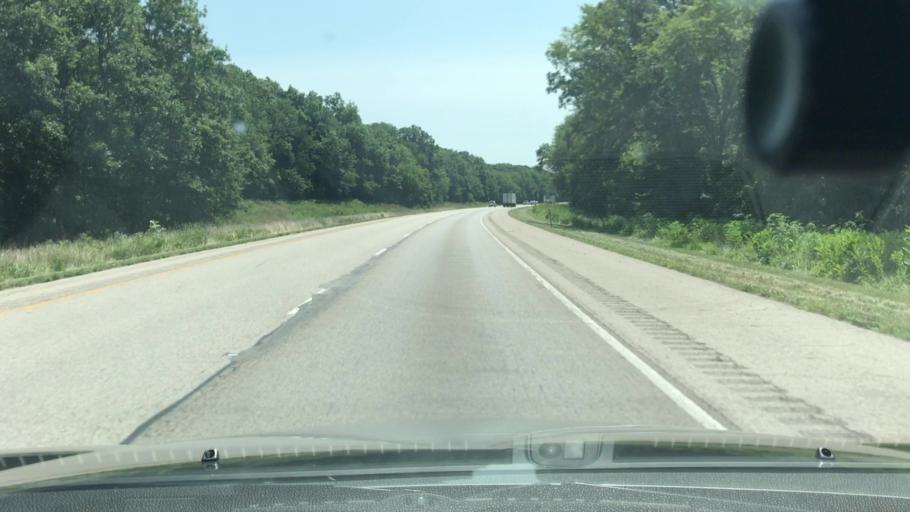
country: US
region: Illinois
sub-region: Washington County
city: Nashville
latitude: 38.4065
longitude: -89.4102
